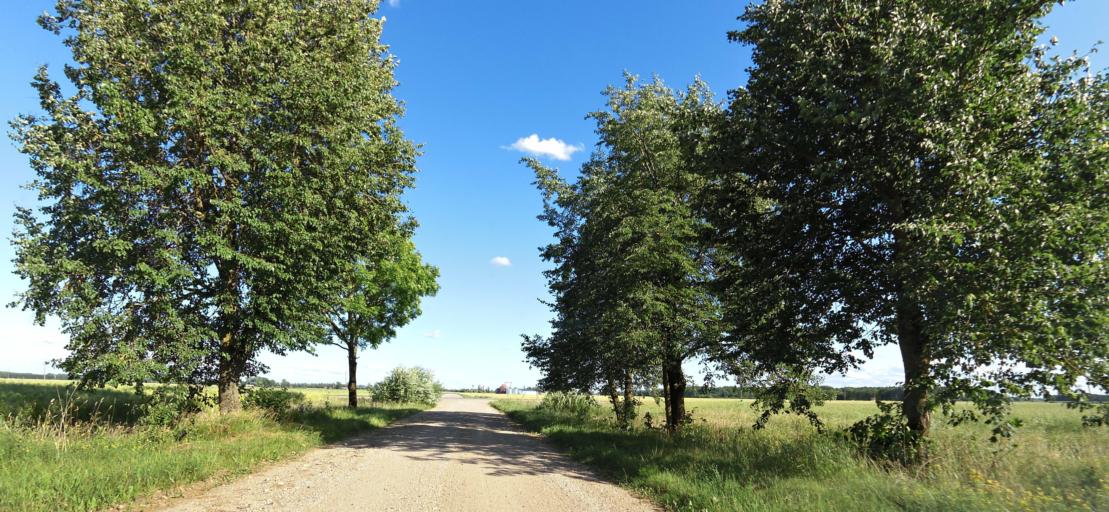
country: LT
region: Panevezys
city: Pasvalys
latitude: 56.1319
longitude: 24.5015
